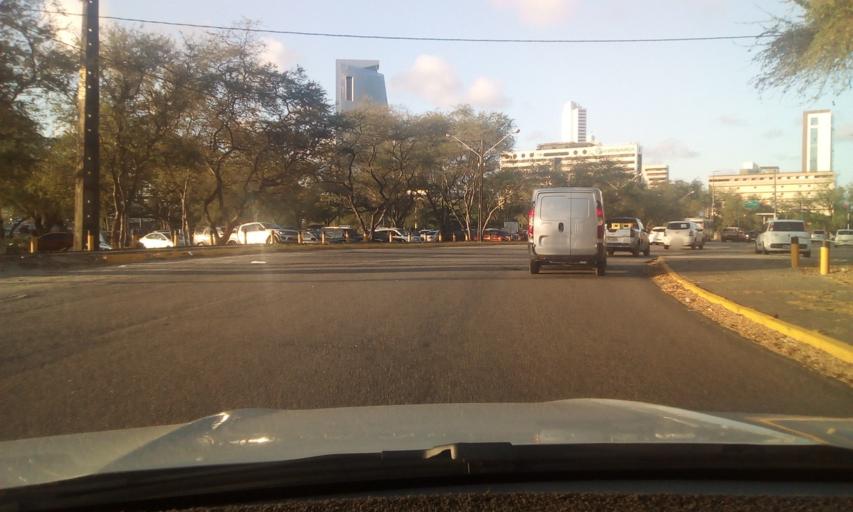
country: BR
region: Pernambuco
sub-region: Recife
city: Recife
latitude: -8.0706
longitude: -34.8958
